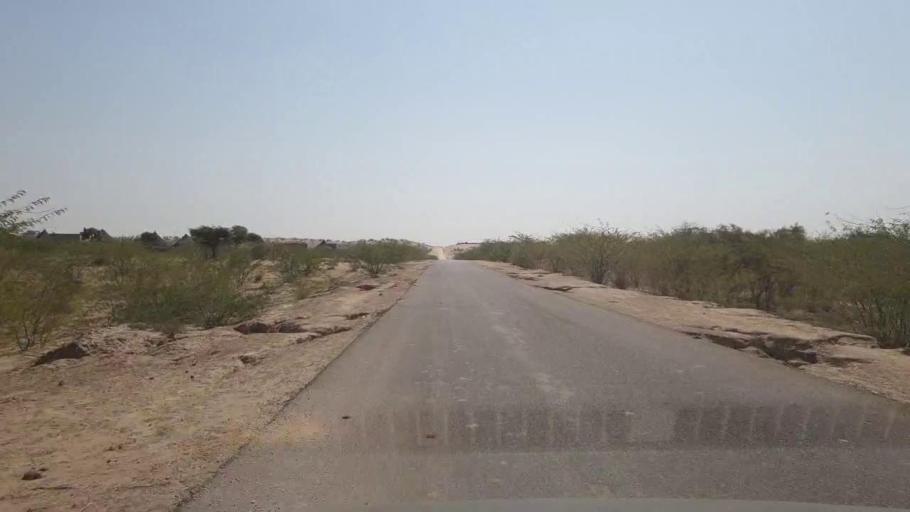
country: PK
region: Sindh
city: Chor
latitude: 25.5805
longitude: 70.1890
